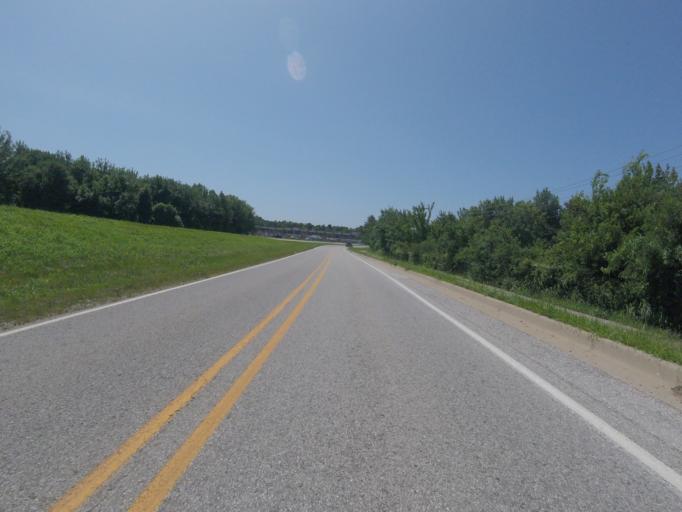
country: US
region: Arkansas
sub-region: Washington County
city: Johnson
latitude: 36.1051
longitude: -94.1828
